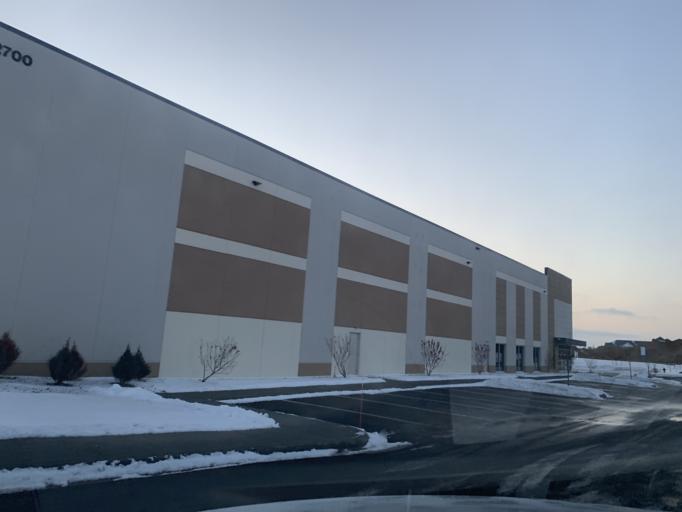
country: US
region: Minnesota
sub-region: Scott County
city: Shakopee
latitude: 44.7947
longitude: -93.4880
